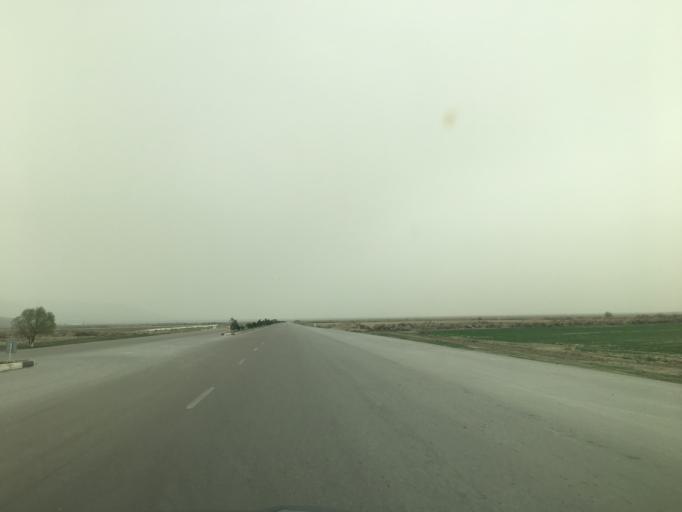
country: TM
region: Ahal
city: Baharly
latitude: 38.3295
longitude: 57.5822
